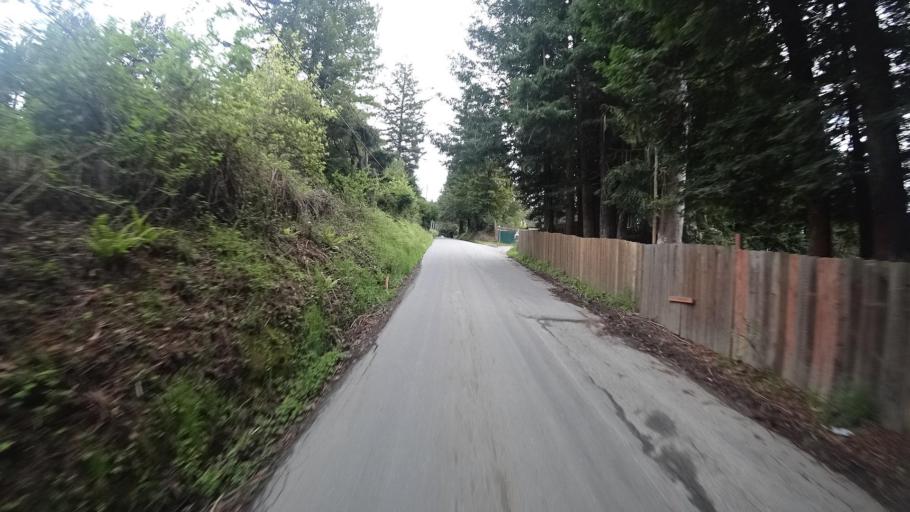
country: US
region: California
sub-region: Humboldt County
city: Blue Lake
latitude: 40.8975
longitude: -124.0060
